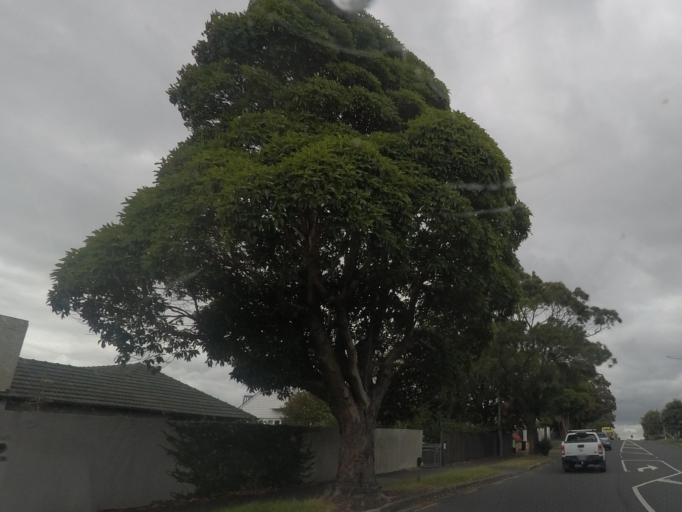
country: NZ
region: Auckland
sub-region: Auckland
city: Tamaki
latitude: -36.8661
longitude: 174.8449
